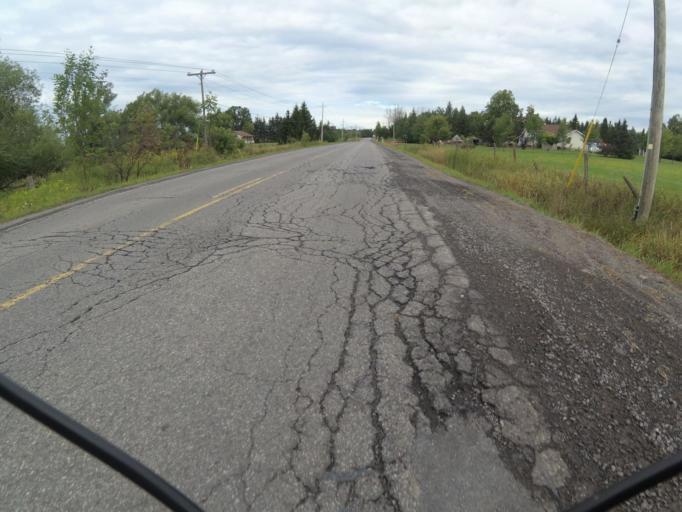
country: CA
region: Ontario
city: Bourget
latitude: 45.3874
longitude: -75.2769
